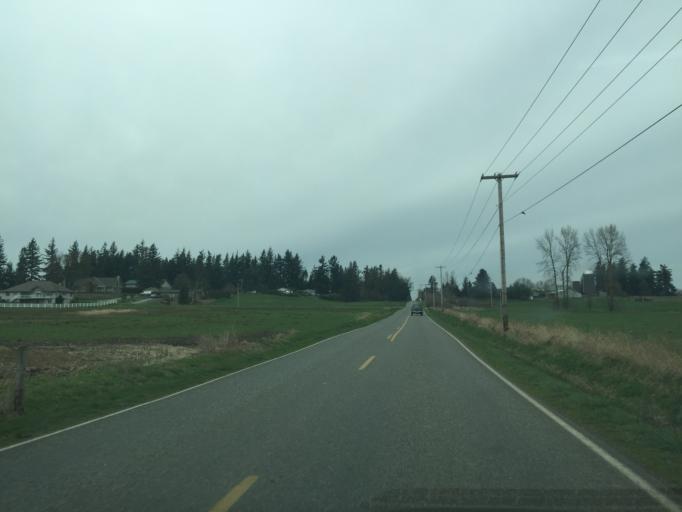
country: US
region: Washington
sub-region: Whatcom County
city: Lynden
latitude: 48.9545
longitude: -122.4077
